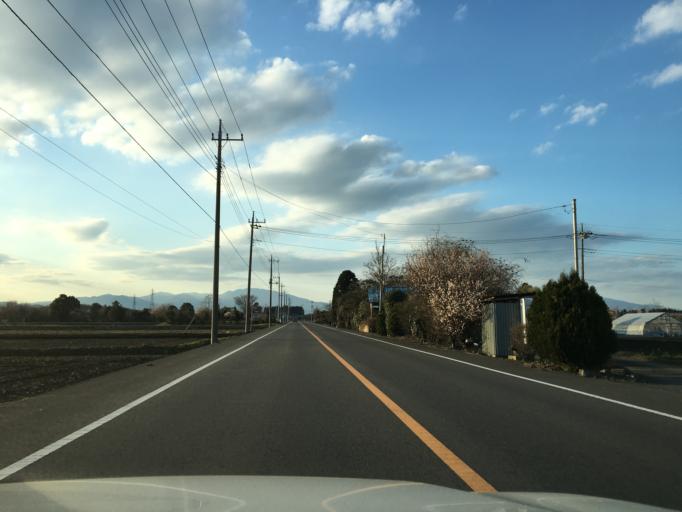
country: JP
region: Tochigi
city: Otawara
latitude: 36.8791
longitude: 140.0667
